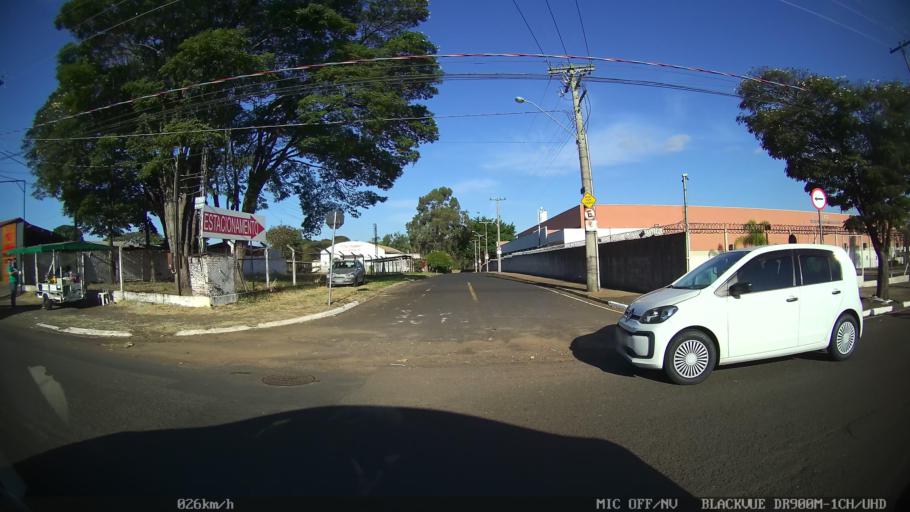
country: BR
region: Sao Paulo
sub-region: Franca
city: Franca
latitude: -20.5157
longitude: -47.3795
